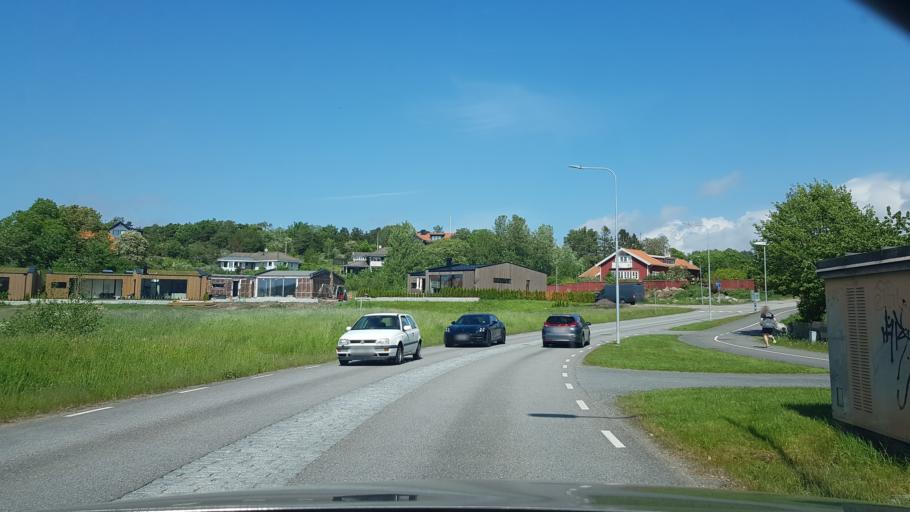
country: SE
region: Vaestra Goetaland
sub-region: Goteborg
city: Billdal
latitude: 57.5988
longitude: 11.9267
